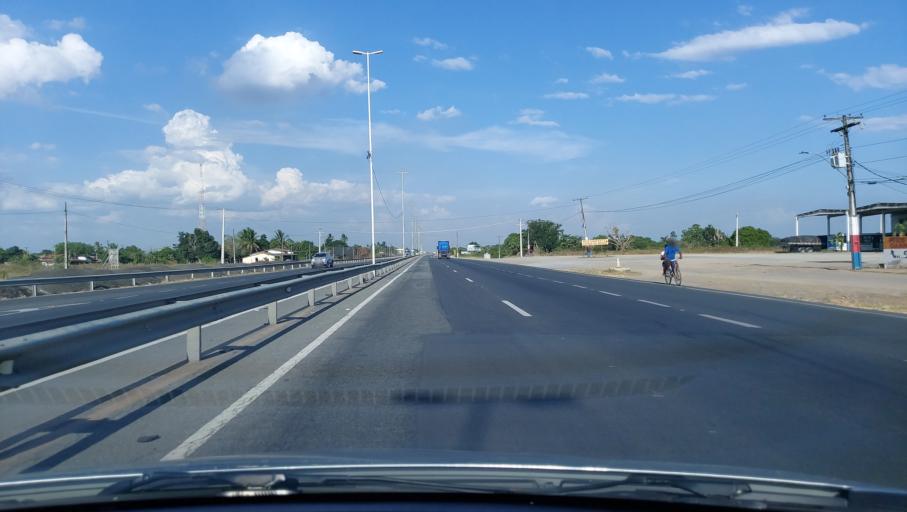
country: BR
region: Bahia
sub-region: Santo Estevao
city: Santo Estevao
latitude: -12.4441
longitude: -39.2377
